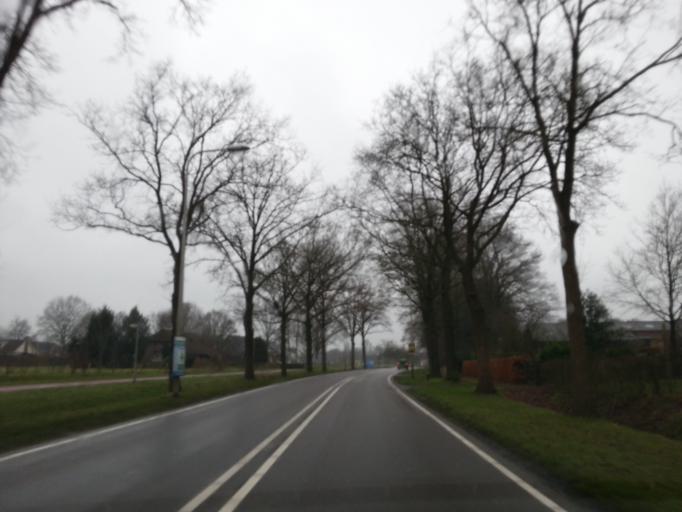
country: NL
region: Overijssel
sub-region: Gemeente Dalfsen
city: Dalfsen
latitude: 52.5187
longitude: 6.2601
